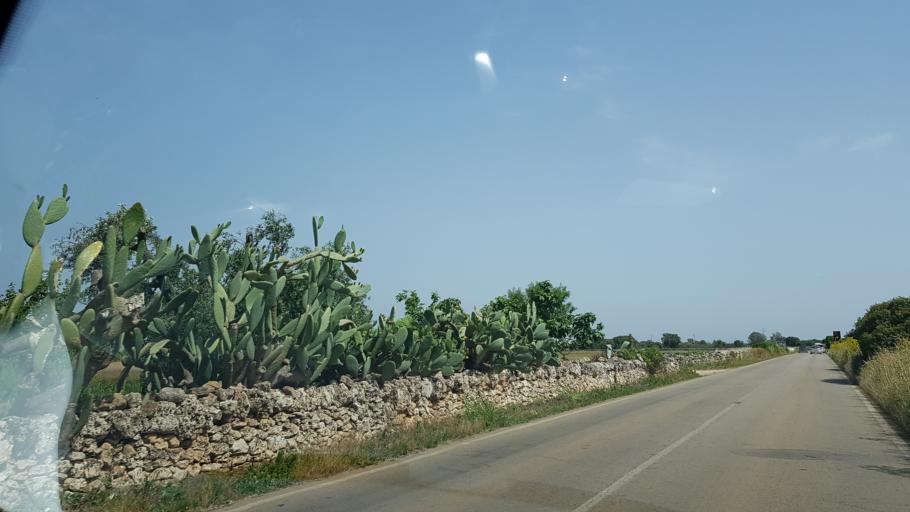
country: IT
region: Apulia
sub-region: Provincia di Lecce
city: Porto Cesareo
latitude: 40.3217
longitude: 17.8568
